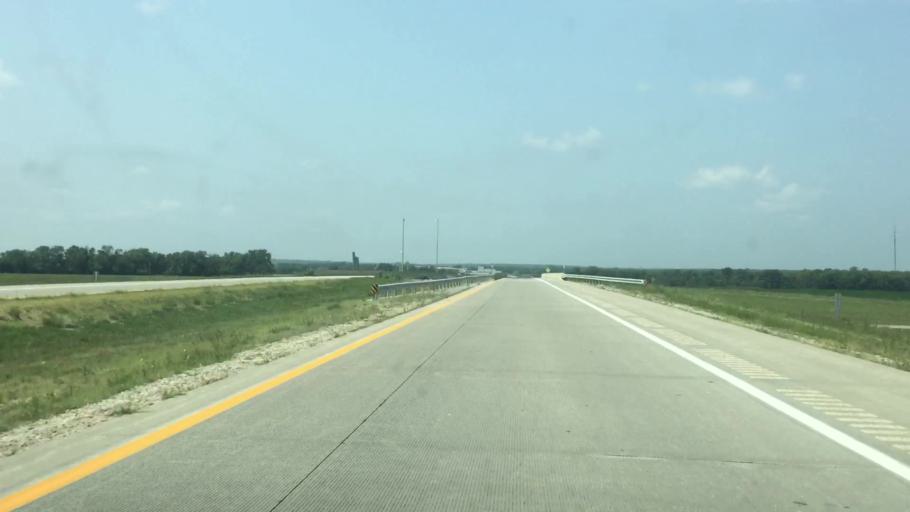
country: US
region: Kansas
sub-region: Franklin County
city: Ottawa
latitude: 38.6369
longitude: -95.2216
